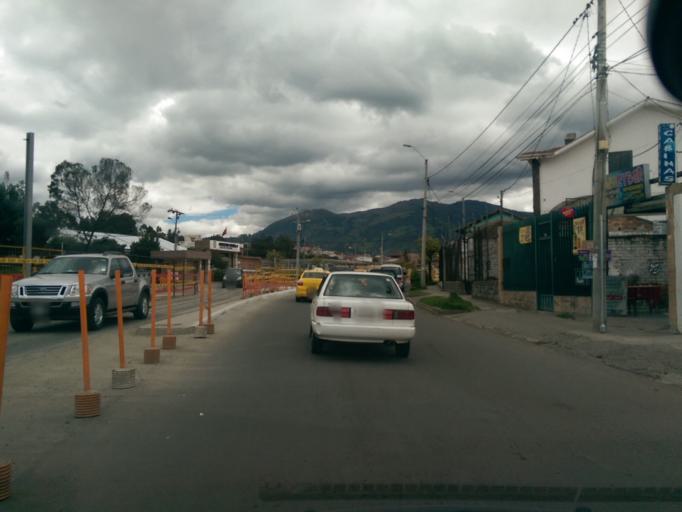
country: EC
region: Azuay
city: Cuenca
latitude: -2.9032
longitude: -79.0264
